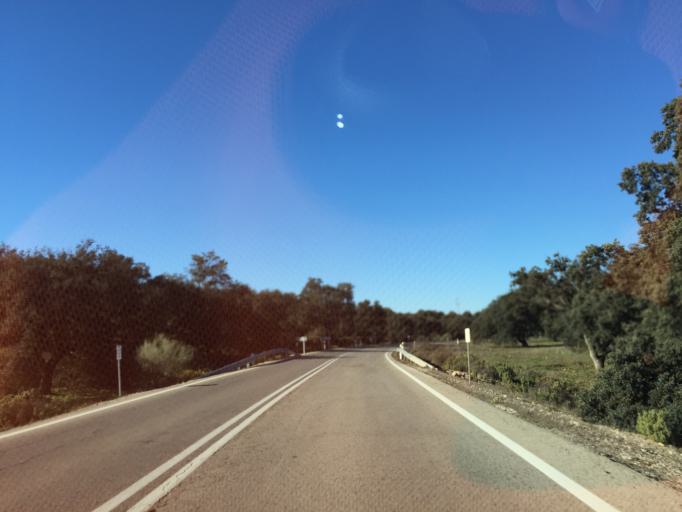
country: ES
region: Andalusia
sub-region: Provincia de Malaga
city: Arriate
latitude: 36.8267
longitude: -5.0903
